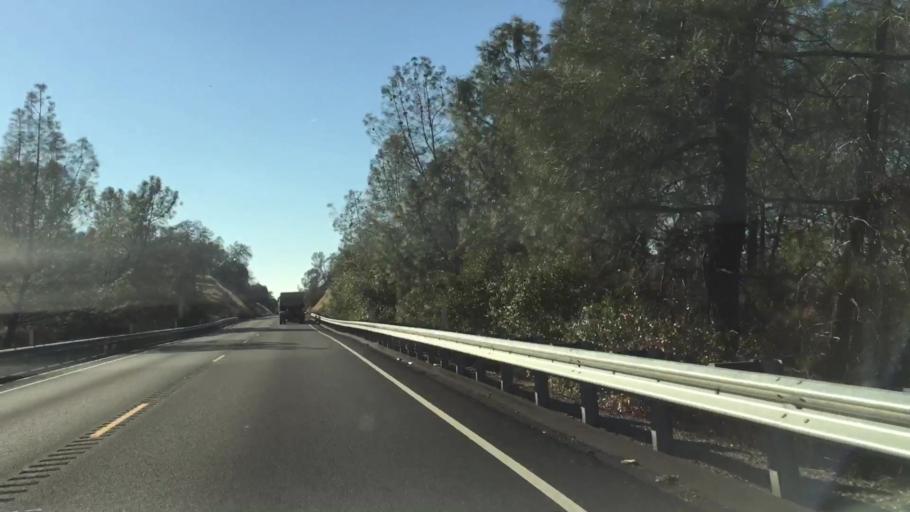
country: US
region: California
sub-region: Butte County
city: Paradise
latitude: 39.6442
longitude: -121.5684
